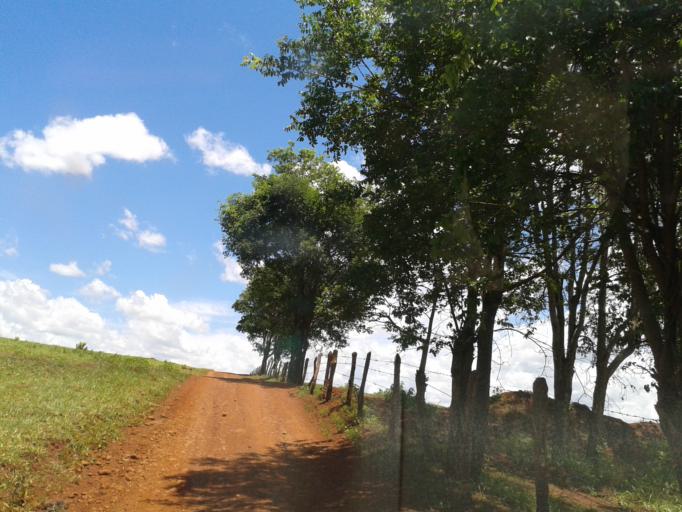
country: BR
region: Minas Gerais
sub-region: Centralina
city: Centralina
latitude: -18.6957
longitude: -49.1919
